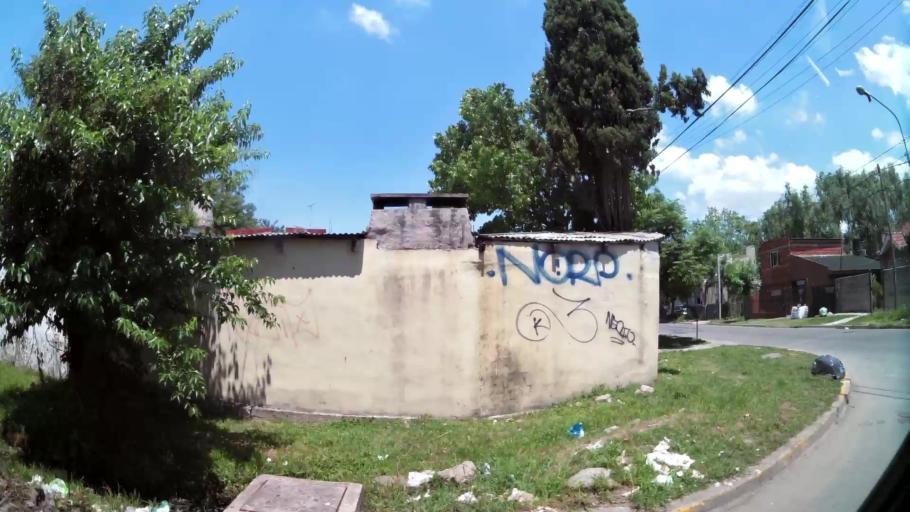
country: AR
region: Buenos Aires
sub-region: Partido de Tigre
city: Tigre
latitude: -34.4259
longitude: -58.5978
